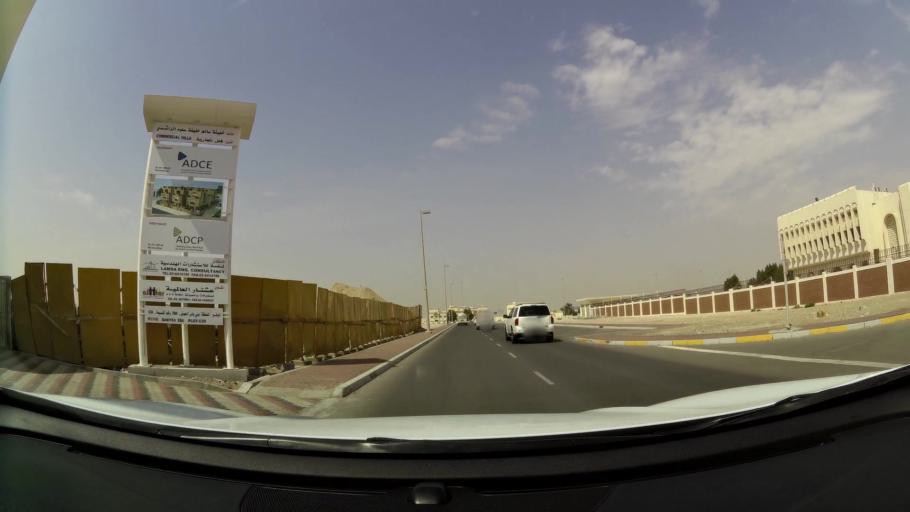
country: AE
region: Abu Dhabi
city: Abu Dhabi
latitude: 24.2980
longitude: 54.6335
